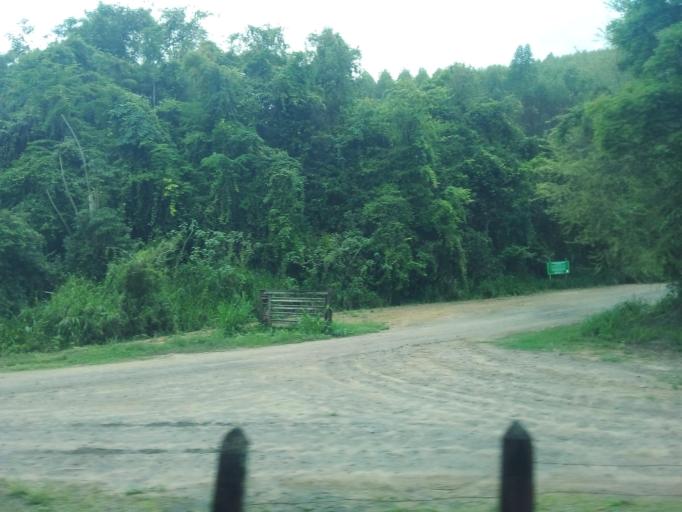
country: BR
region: Minas Gerais
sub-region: Nova Era
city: Nova Era
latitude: -19.7255
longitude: -42.9854
